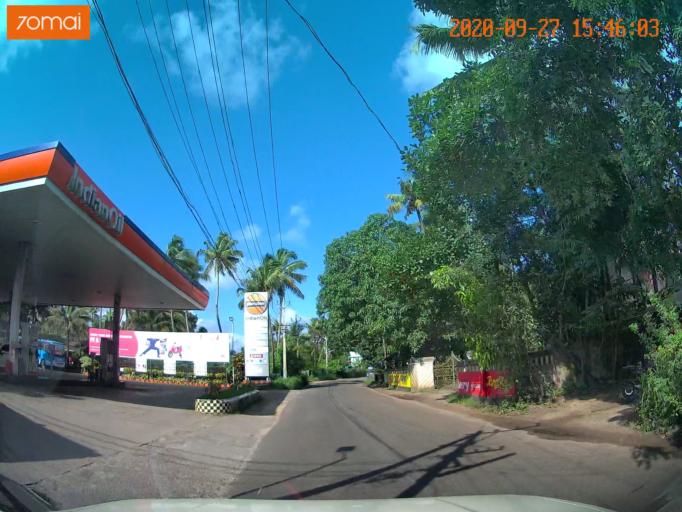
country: IN
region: Kerala
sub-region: Thrissur District
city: Thanniyam
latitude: 10.4794
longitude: 76.1193
